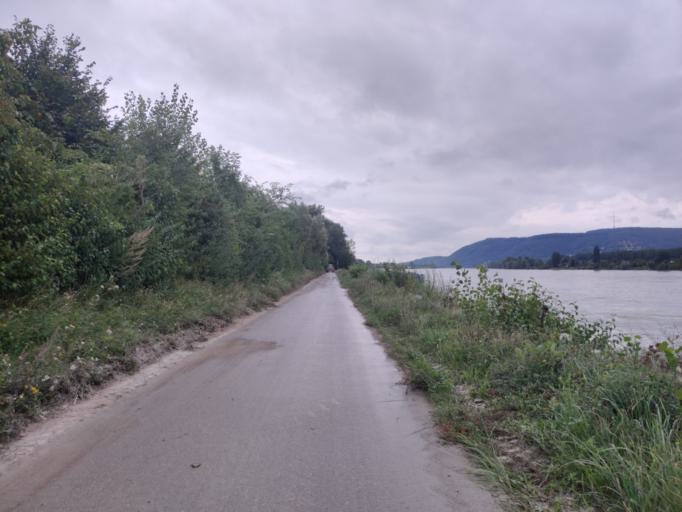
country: AT
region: Lower Austria
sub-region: Politischer Bezirk Korneuburg
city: Bisamberg
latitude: 48.3221
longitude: 16.3378
